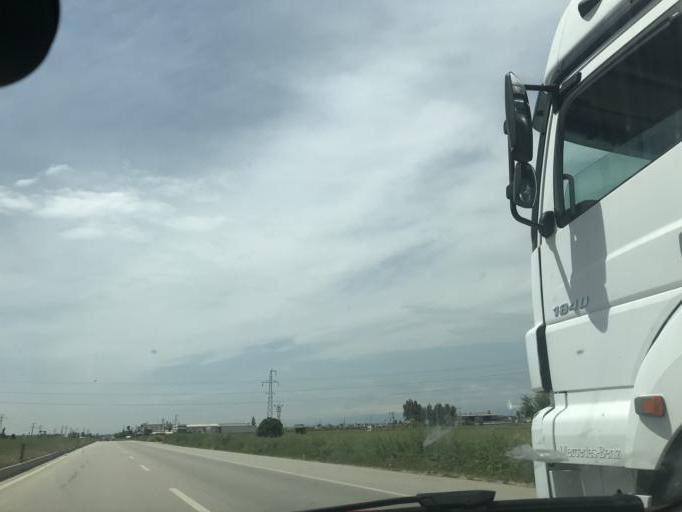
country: TR
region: Adana
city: Yuregir
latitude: 36.9792
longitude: 35.4584
